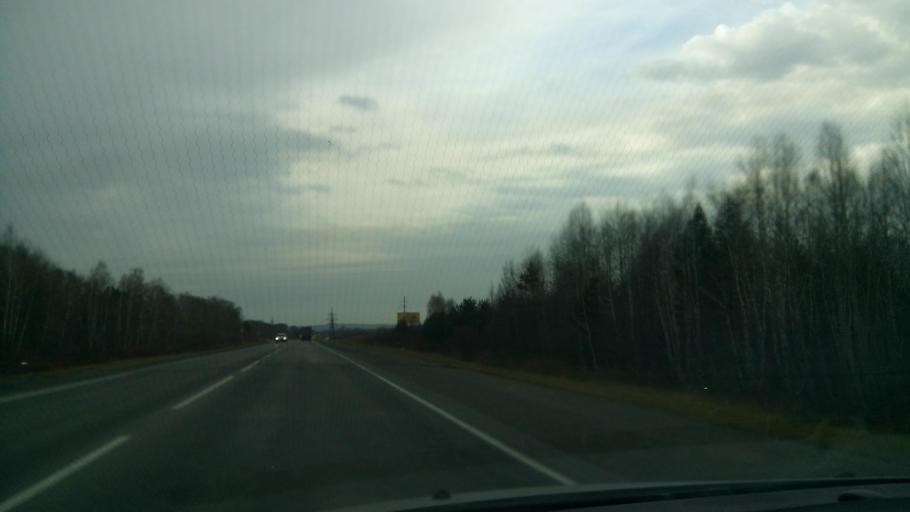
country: RU
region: Sverdlovsk
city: Obukhovskoye
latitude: 56.8477
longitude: 62.5971
